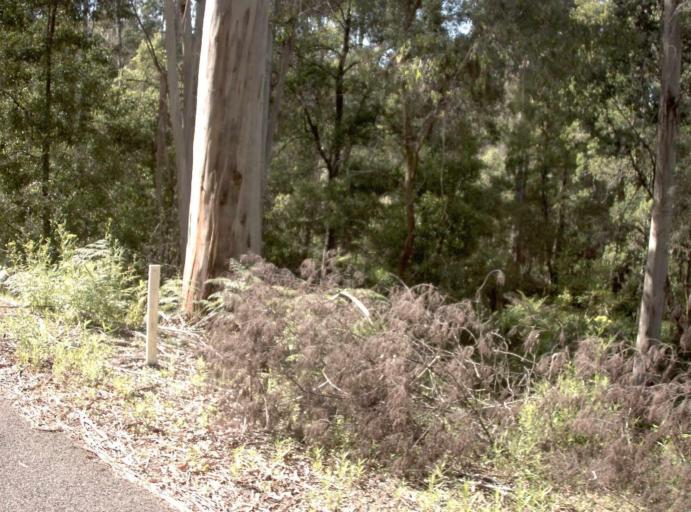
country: AU
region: New South Wales
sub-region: Bombala
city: Bombala
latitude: -37.3535
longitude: 148.6897
